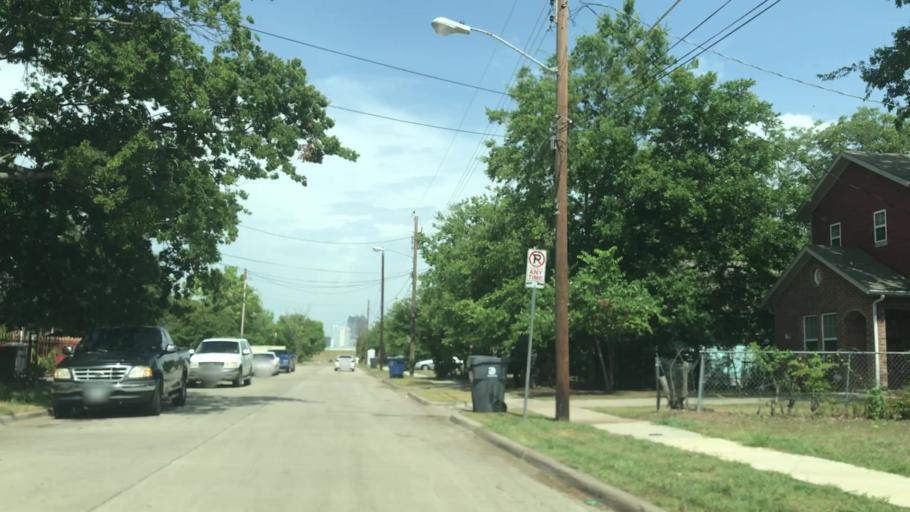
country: US
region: Texas
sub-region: Dallas County
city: Dallas
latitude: 32.7887
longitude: -96.8469
